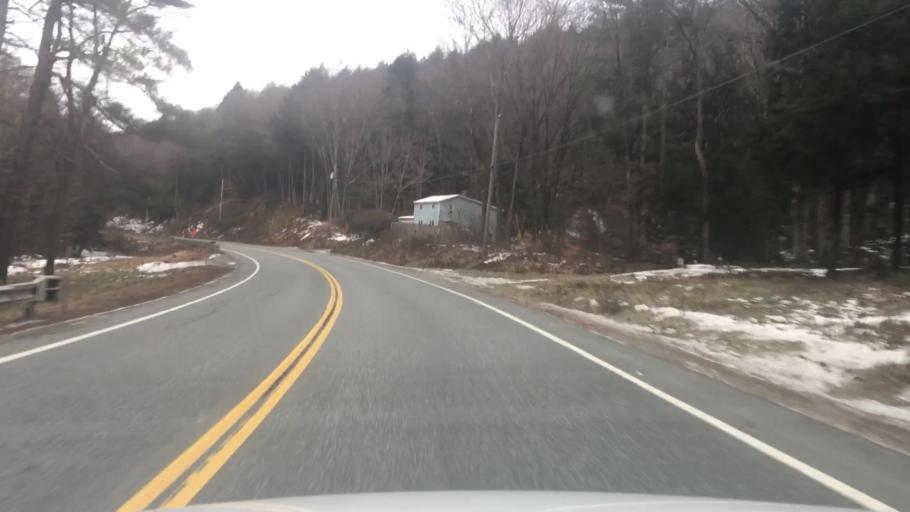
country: US
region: New Hampshire
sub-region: Cheshire County
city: Westmoreland
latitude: 42.9898
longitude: -72.4279
